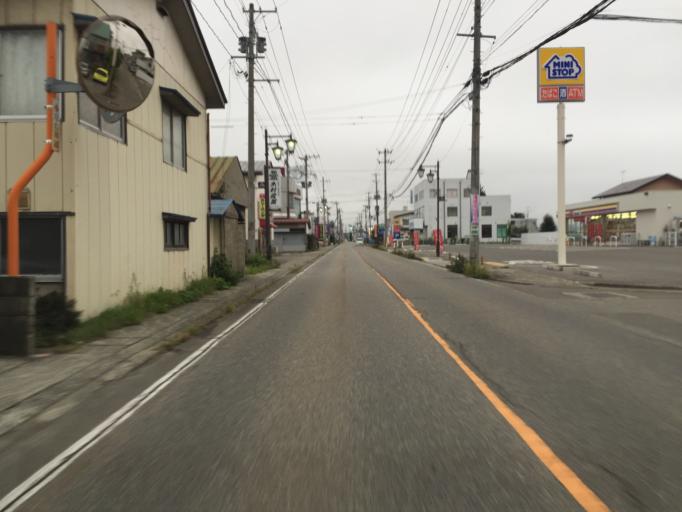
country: JP
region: Fukushima
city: Kitakata
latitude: 37.4674
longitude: 139.9229
